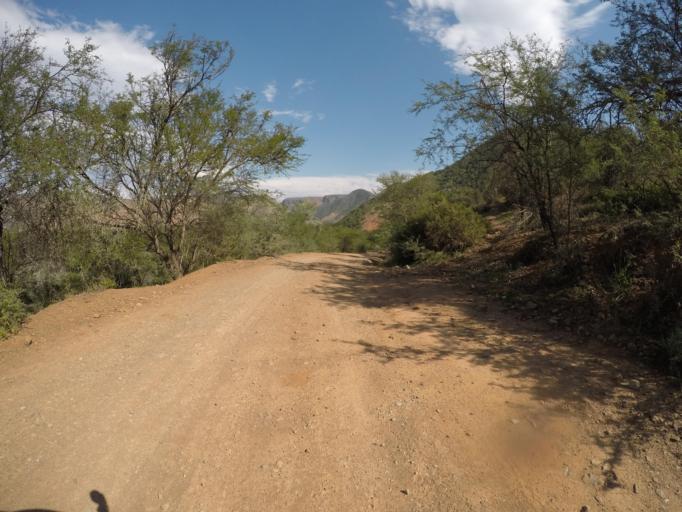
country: ZA
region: Eastern Cape
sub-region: Cacadu District Municipality
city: Kareedouw
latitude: -33.6592
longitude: 24.3990
